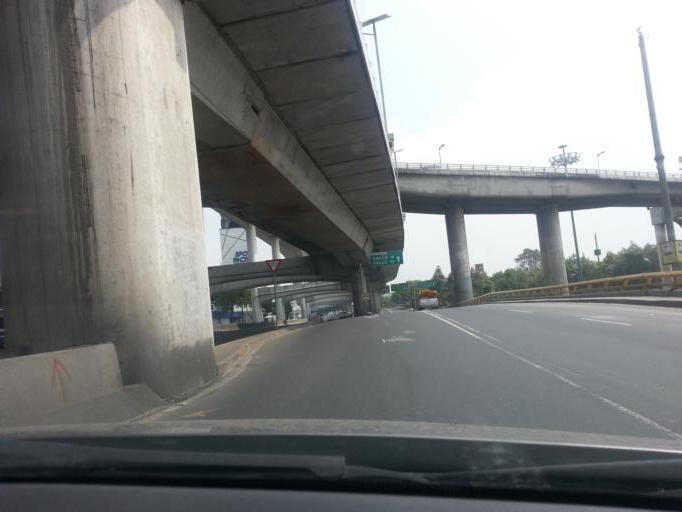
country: MX
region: Mexico City
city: Alvaro Obregon
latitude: 19.3844
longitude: -99.1909
